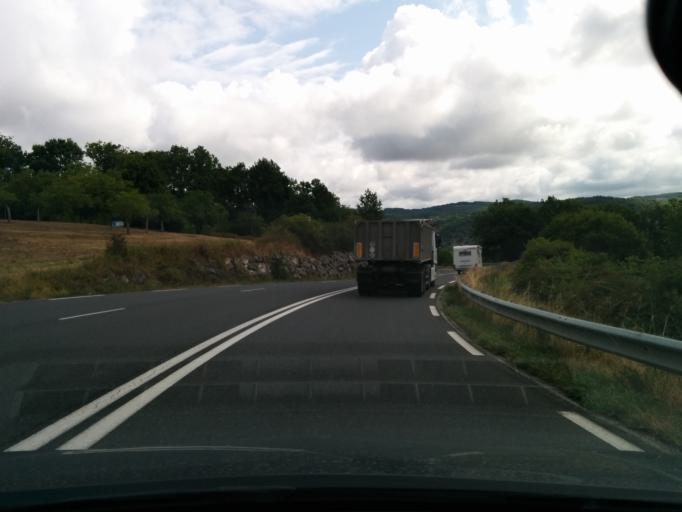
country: FR
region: Midi-Pyrenees
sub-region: Departement du Lot
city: Souillac
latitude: 44.8679
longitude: 1.4797
